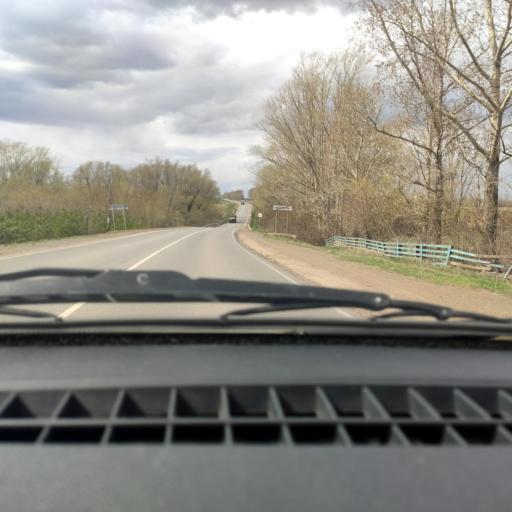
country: RU
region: Bashkortostan
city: Alekseyevka
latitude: 55.0523
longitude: 55.1263
